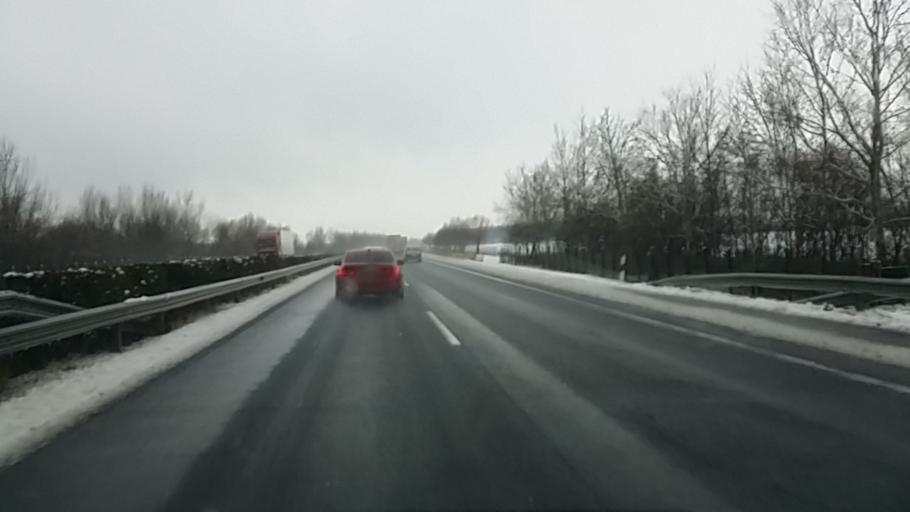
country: HU
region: Gyor-Moson-Sopron
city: Kimle
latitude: 47.7999
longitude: 17.3093
